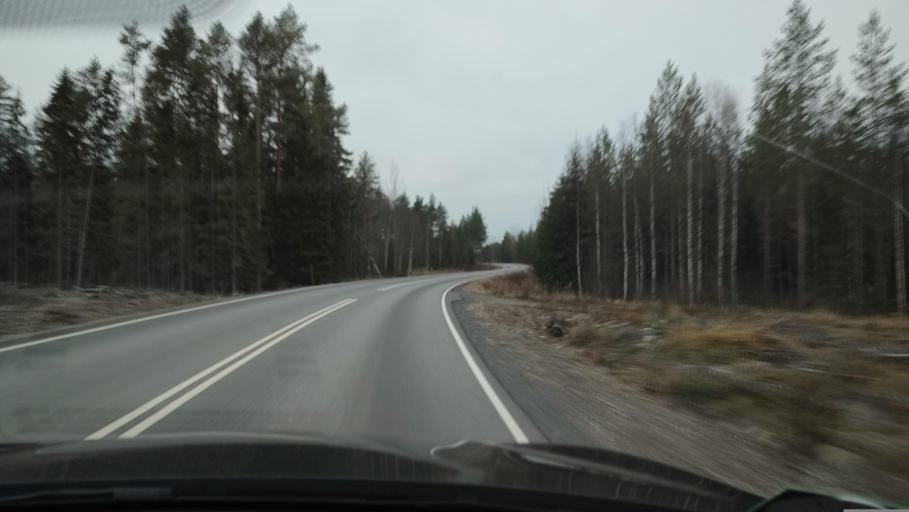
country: FI
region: Southern Ostrobothnia
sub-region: Suupohja
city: Karijoki
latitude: 62.2766
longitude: 21.5887
